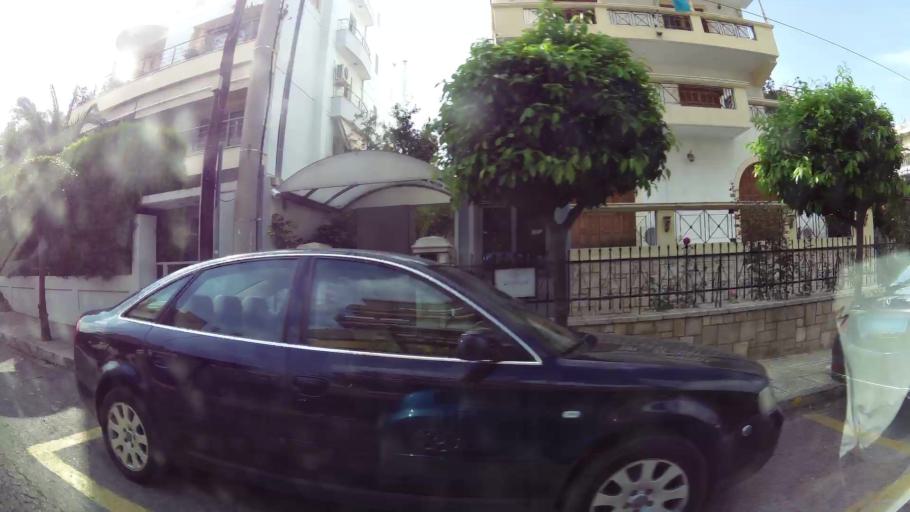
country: GR
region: Attica
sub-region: Nomarchia Athinas
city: Cholargos
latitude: 37.9934
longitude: 23.8016
